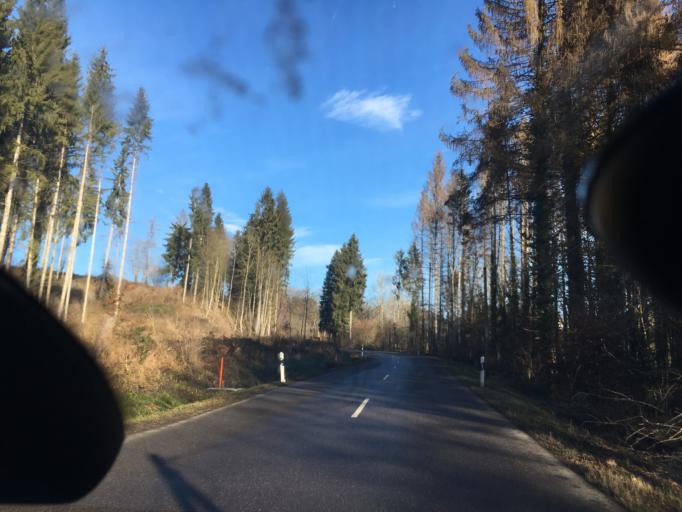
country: DE
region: Baden-Wuerttemberg
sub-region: Freiburg Region
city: Gorwihl
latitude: 47.6295
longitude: 8.1076
